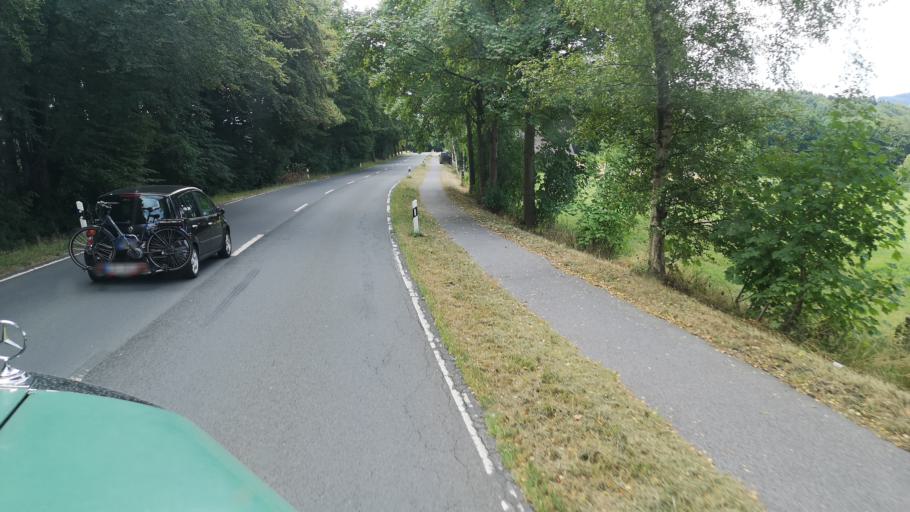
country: DE
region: North Rhine-Westphalia
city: Huckeswagen
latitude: 51.1629
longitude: 7.3575
